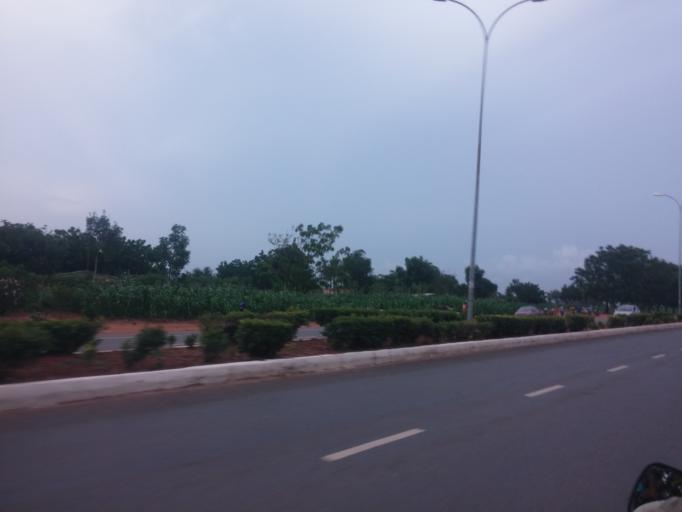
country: TG
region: Maritime
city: Lome
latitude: 6.1945
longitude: 1.2112
